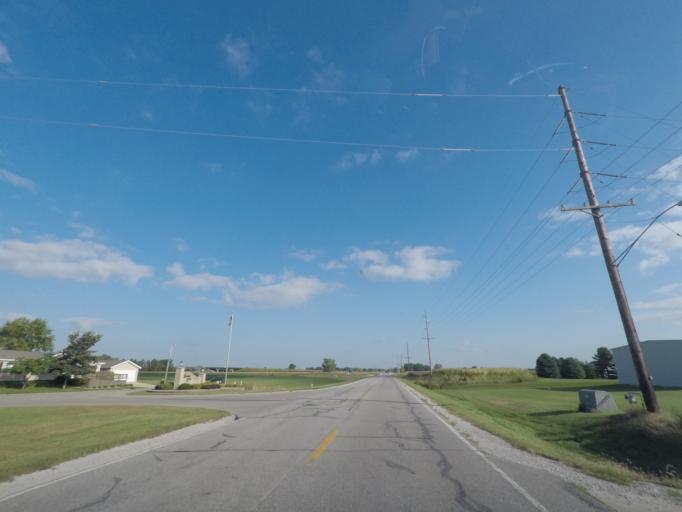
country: US
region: Iowa
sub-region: Story County
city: Nevada
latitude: 42.0018
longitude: -93.4628
